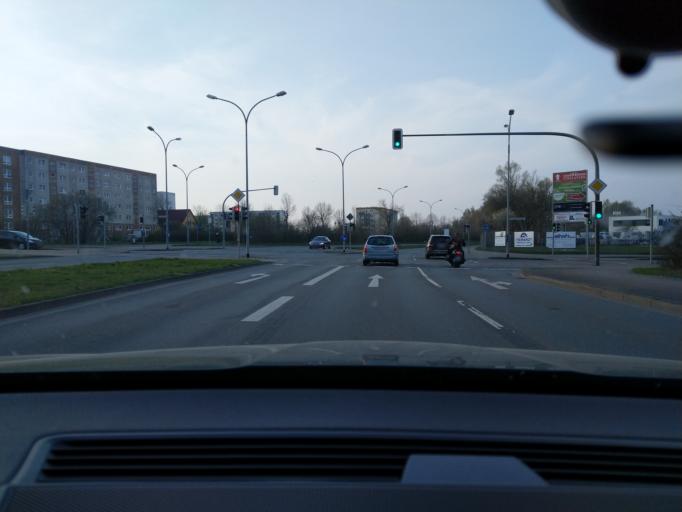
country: DE
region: Mecklenburg-Vorpommern
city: Stralsund
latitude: 54.3105
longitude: 13.0442
